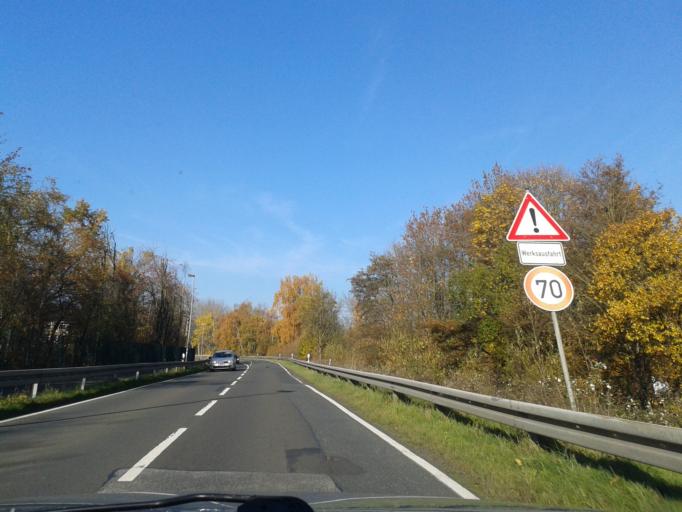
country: DE
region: Hesse
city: Dillenburg
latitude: 50.8189
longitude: 8.3375
